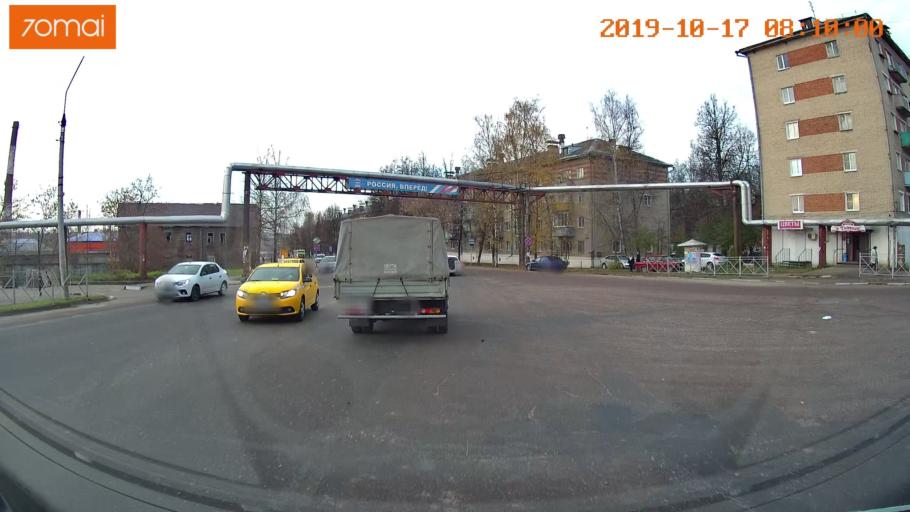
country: RU
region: Vladimir
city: Kol'chugino
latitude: 56.3100
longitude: 39.3791
